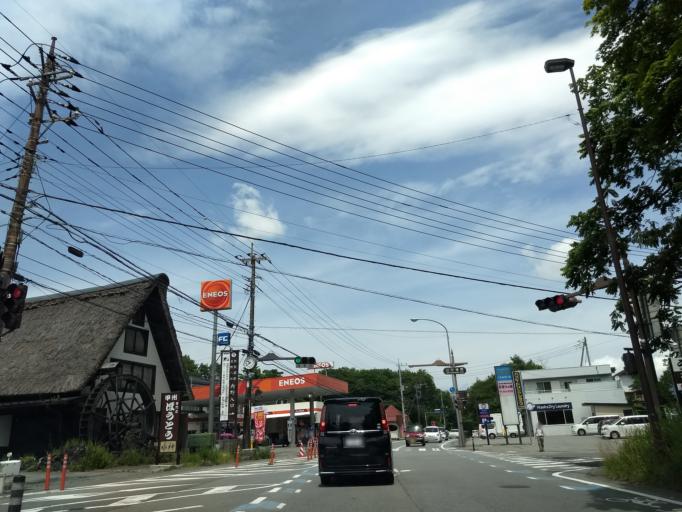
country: JP
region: Shizuoka
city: Gotemba
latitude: 35.4290
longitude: 138.8457
